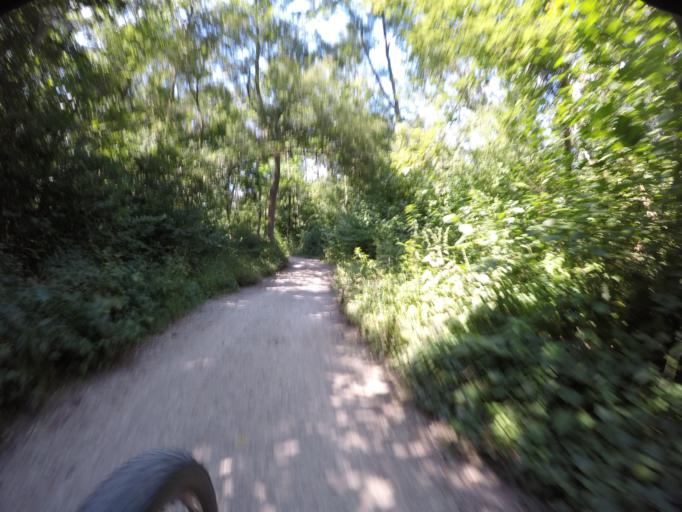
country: AT
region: Lower Austria
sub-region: Politischer Bezirk Wien-Umgebung
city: Schwechat
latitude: 48.1891
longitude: 16.4893
